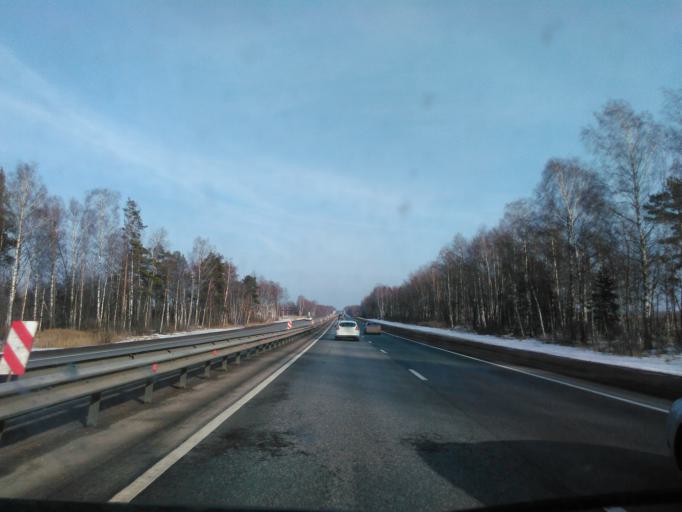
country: RU
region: Smolensk
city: Kholm-Zhirkovskiy
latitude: 55.1850
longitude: 33.7109
